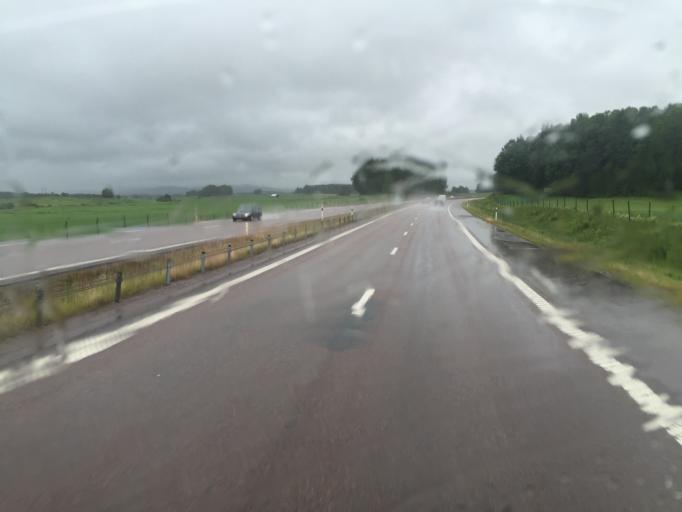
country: SE
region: Dalarna
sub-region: Borlange Kommun
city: Ornas
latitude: 60.4981
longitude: 15.5116
